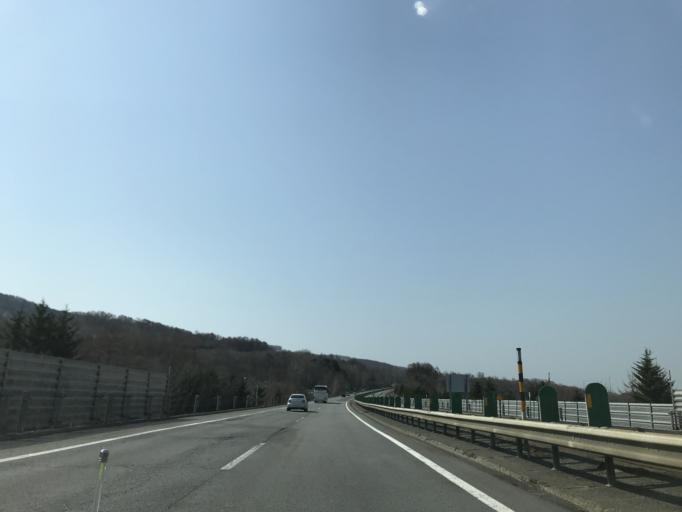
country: JP
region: Hokkaido
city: Bibai
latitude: 43.3265
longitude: 141.8877
